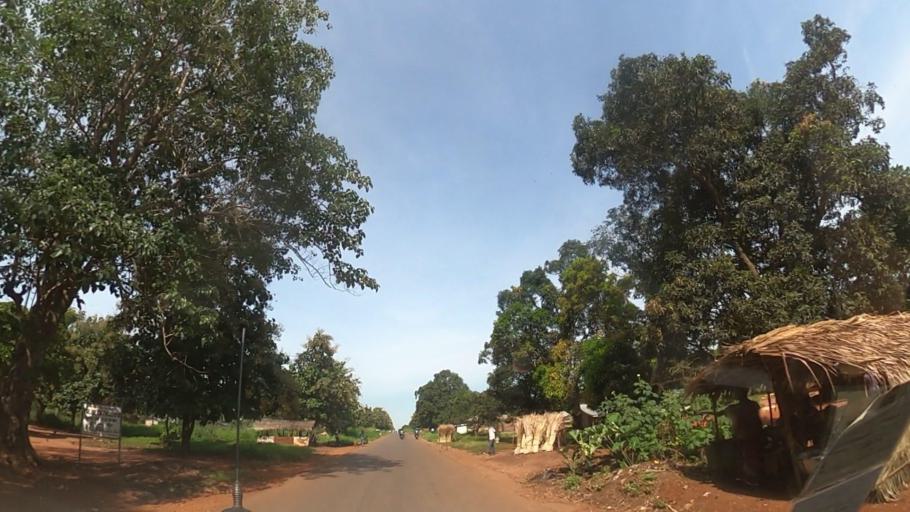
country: CF
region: Ombella-Mpoko
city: Bimbo
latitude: 4.3124
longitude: 18.4772
